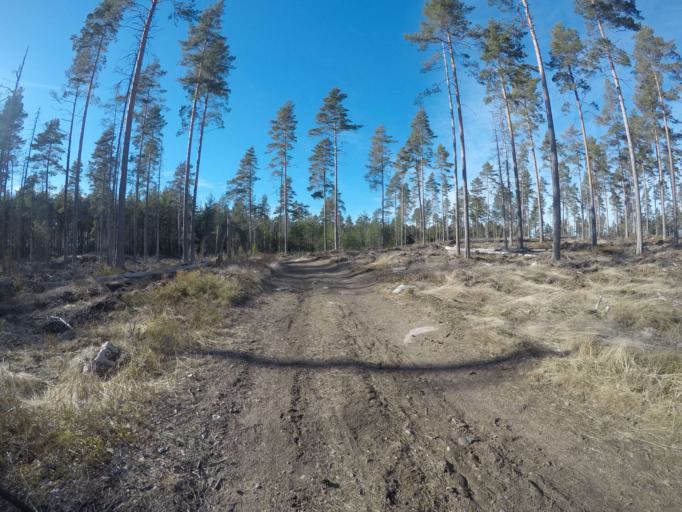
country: SE
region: Soedermanland
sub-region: Eskilstuna Kommun
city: Torshalla
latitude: 59.4253
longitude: 16.4397
